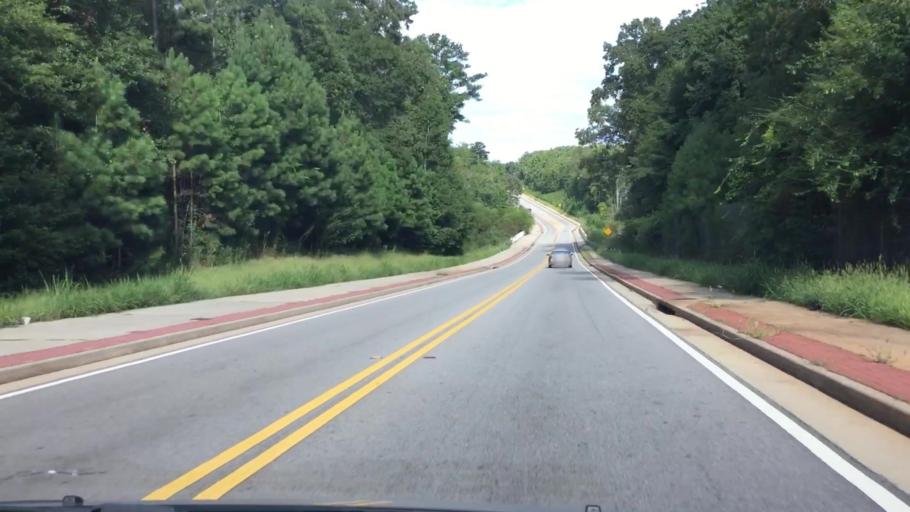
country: US
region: Georgia
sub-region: Clayton County
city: Conley
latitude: 33.6474
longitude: -84.2763
